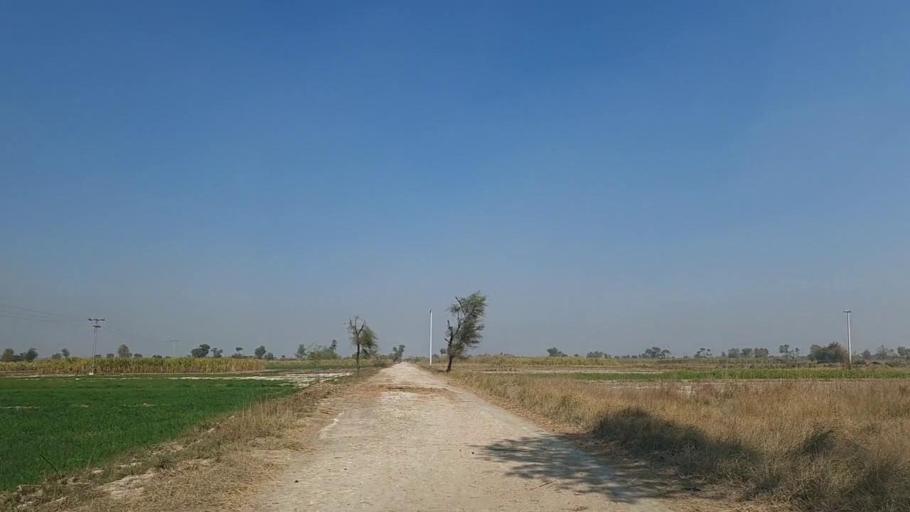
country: PK
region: Sindh
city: Daur
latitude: 26.4889
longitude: 68.3384
